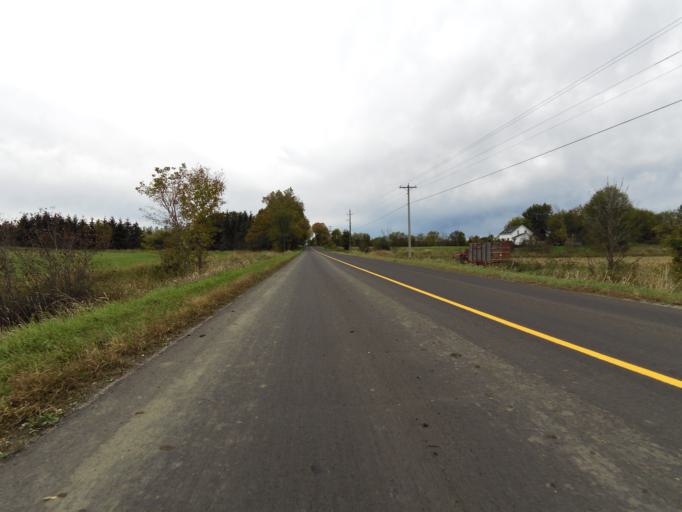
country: US
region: New York
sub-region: Jefferson County
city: Alexandria Bay
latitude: 44.5838
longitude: -76.0324
